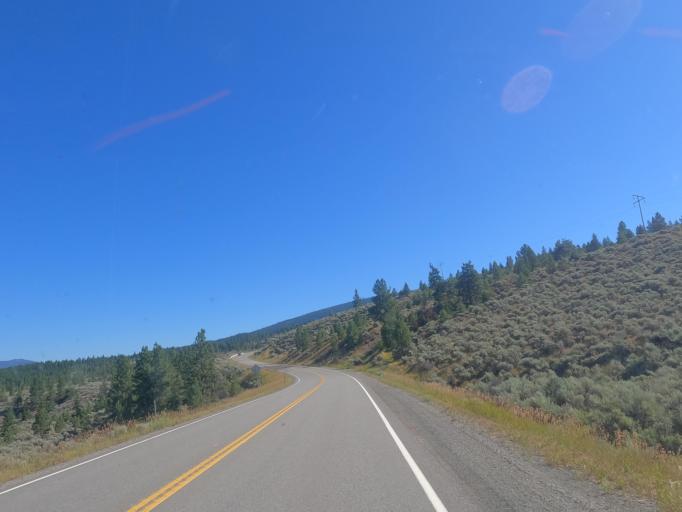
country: CA
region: British Columbia
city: Merritt
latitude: 50.1948
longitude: -120.8509
